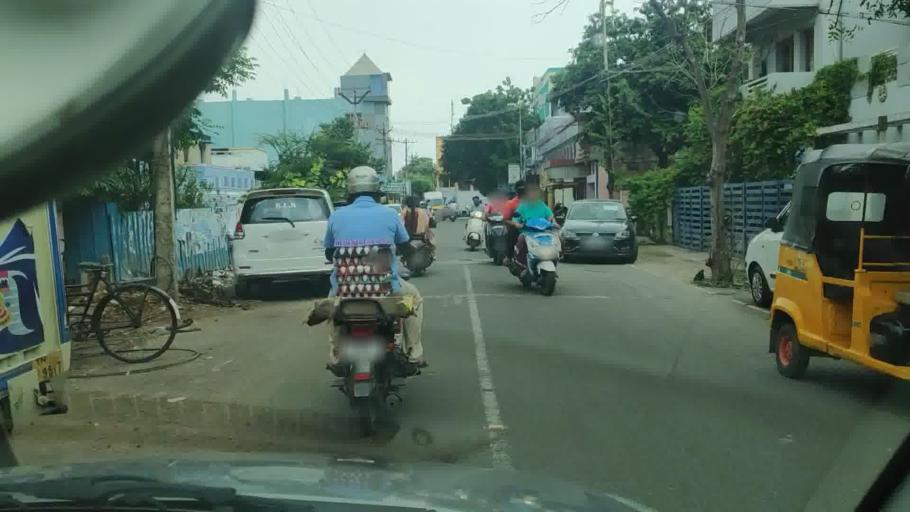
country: IN
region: Tamil Nadu
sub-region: Thiruvallur
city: Ambattur
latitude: 13.1183
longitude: 80.1507
